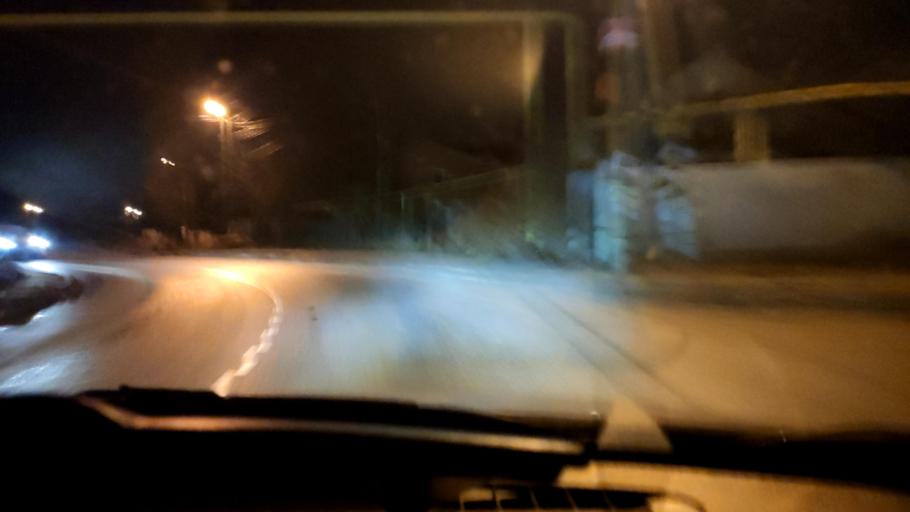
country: RU
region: Voronezj
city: Somovo
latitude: 51.7393
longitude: 39.3461
